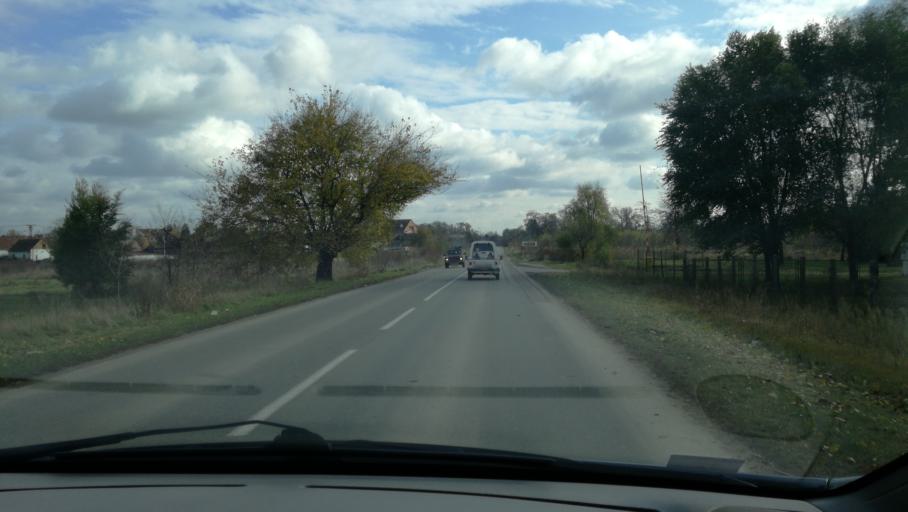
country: RS
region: Autonomna Pokrajina Vojvodina
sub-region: Severnobanatski Okrug
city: Kikinda
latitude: 45.8219
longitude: 20.4326
